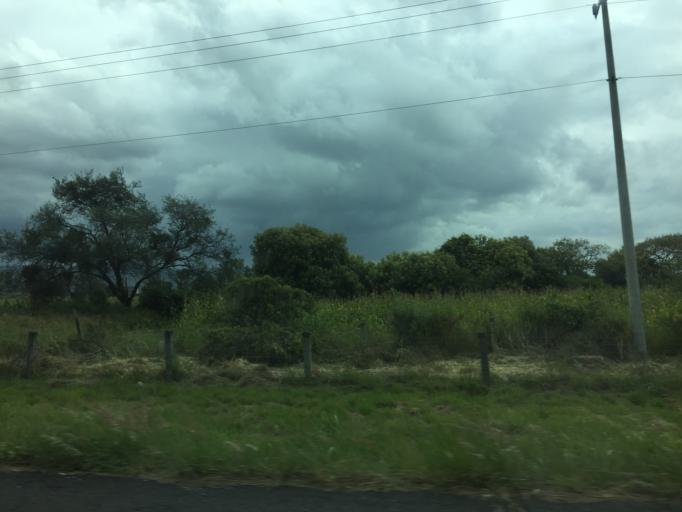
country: MX
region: Jalisco
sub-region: Zapotlanejo
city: La Mezquitera
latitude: 20.5958
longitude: -103.1116
